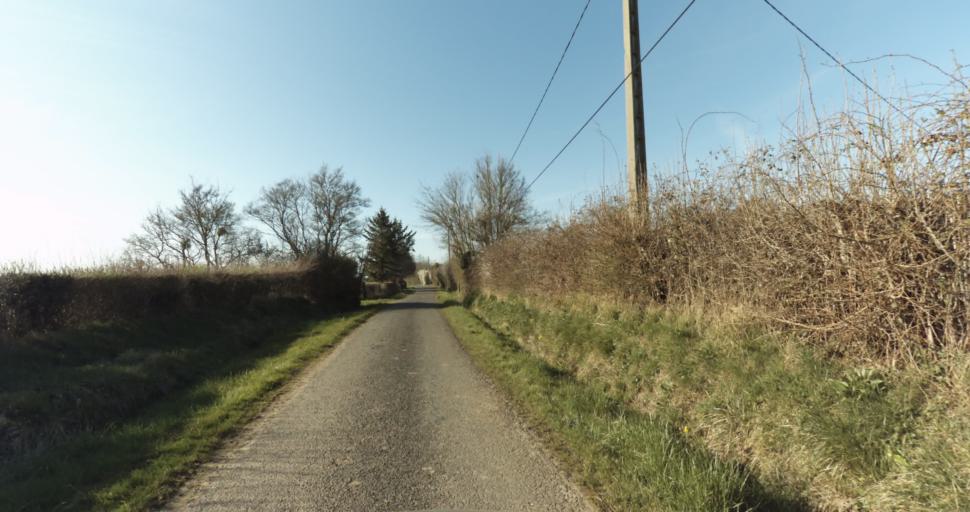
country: FR
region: Lower Normandy
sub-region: Departement du Calvados
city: Saint-Pierre-sur-Dives
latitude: 49.0475
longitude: 0.0249
